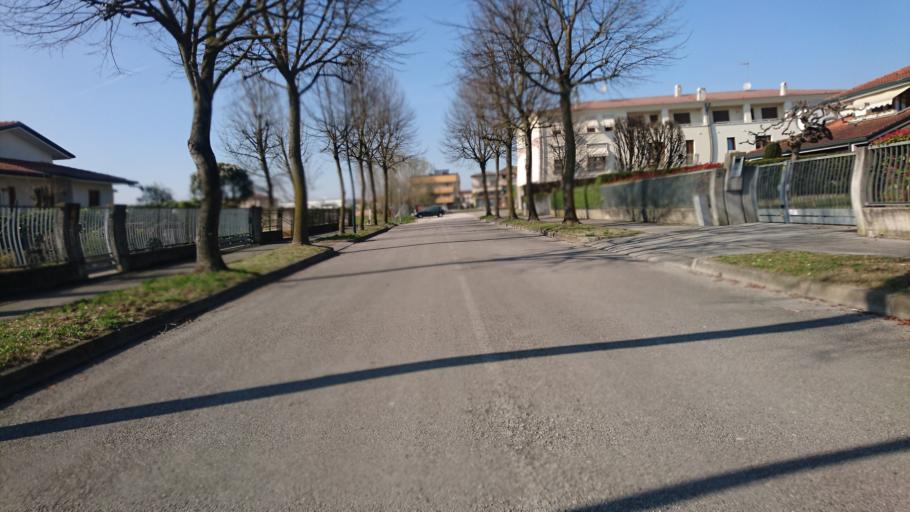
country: IT
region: Veneto
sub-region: Provincia di Padova
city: Vigonza
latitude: 45.4430
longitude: 11.9684
